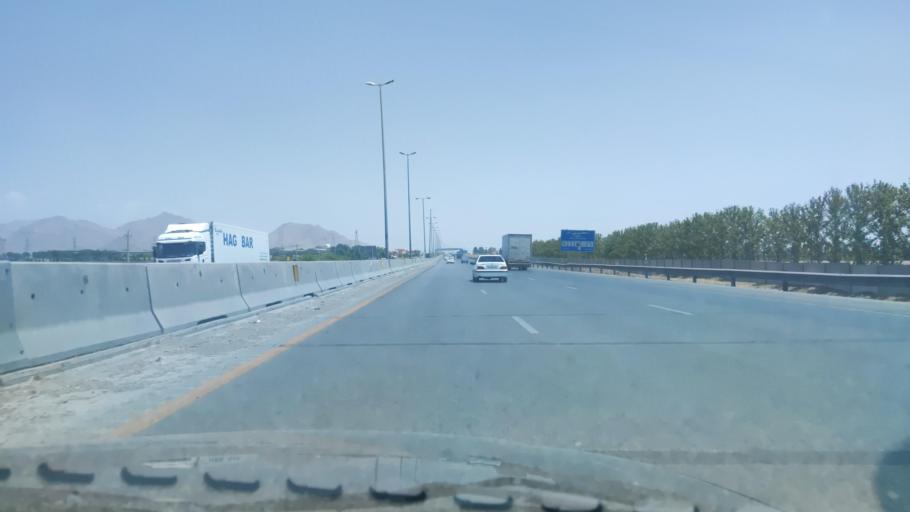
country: IR
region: Qazvin
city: Abyek
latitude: 36.0970
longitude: 50.4322
